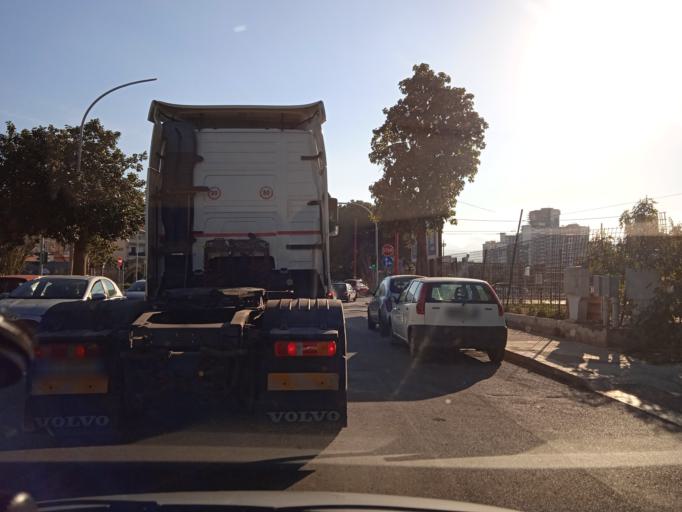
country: IT
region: Sicily
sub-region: Palermo
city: Ciaculli
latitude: 38.1060
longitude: 13.3756
